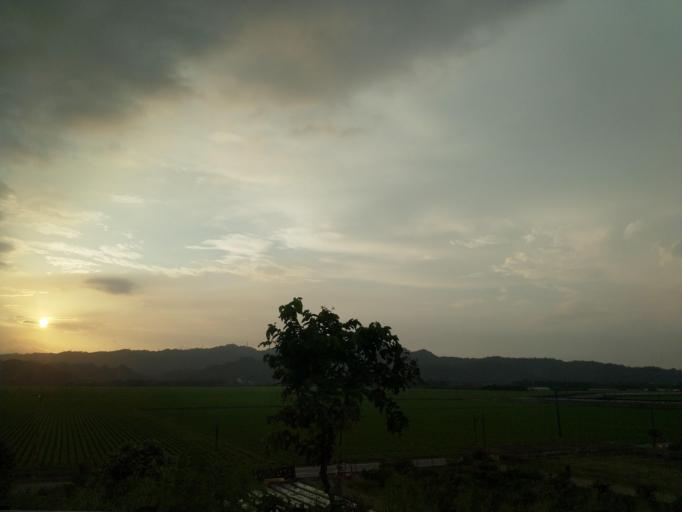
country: TW
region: Taiwan
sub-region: Pingtung
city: Pingtung
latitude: 22.8255
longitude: 120.4881
